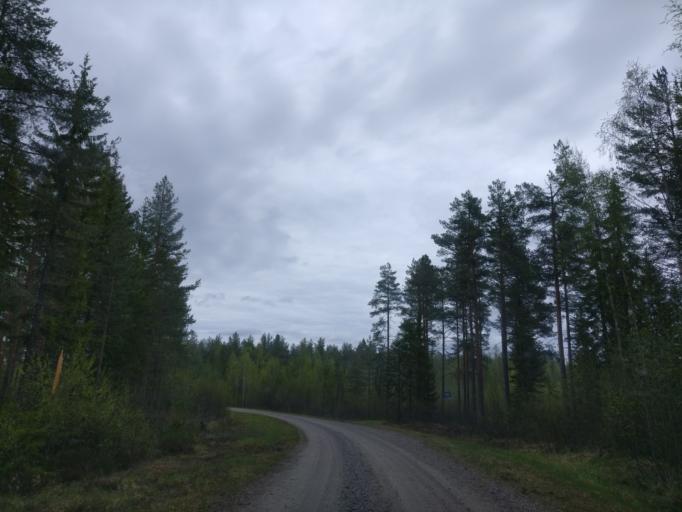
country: SE
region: Gaevleborg
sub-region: Soderhamns Kommun
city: Soderhamn
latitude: 61.4167
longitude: 16.8906
